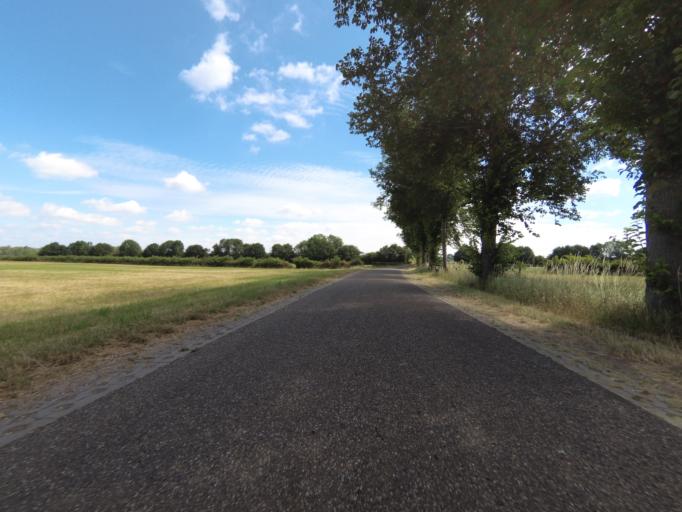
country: NL
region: Gelderland
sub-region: Gemeente Voorst
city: Wilp
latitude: 52.2217
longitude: 6.1610
